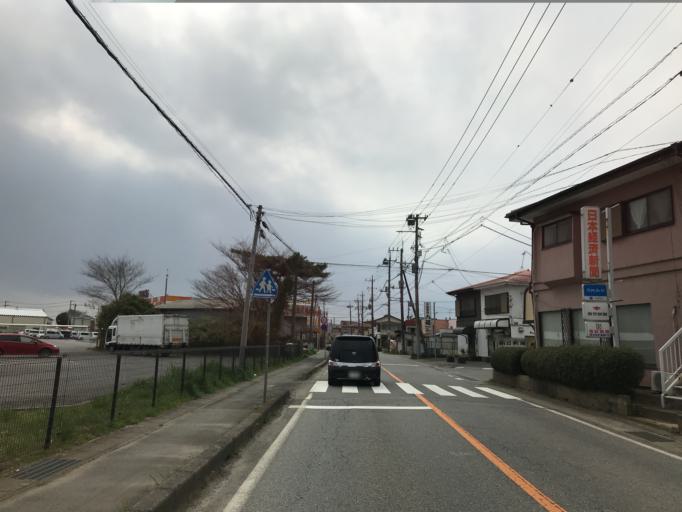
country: JP
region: Ibaraki
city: Ushiku
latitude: 35.9880
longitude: 140.0598
